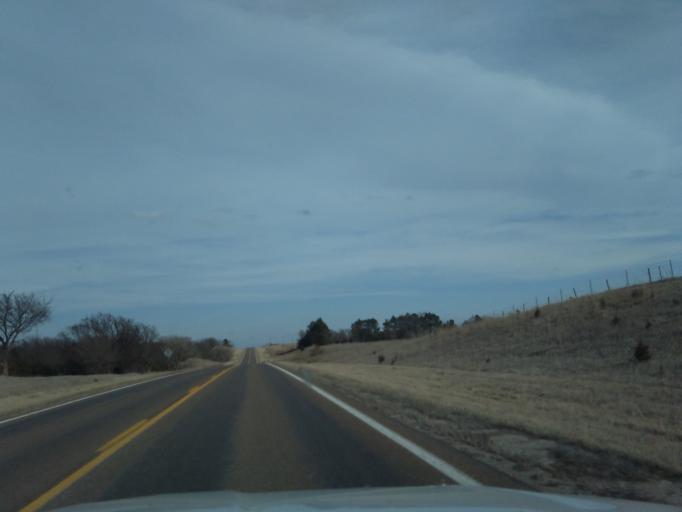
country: US
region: Nebraska
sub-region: Jefferson County
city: Fairbury
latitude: 40.3060
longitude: -97.1744
